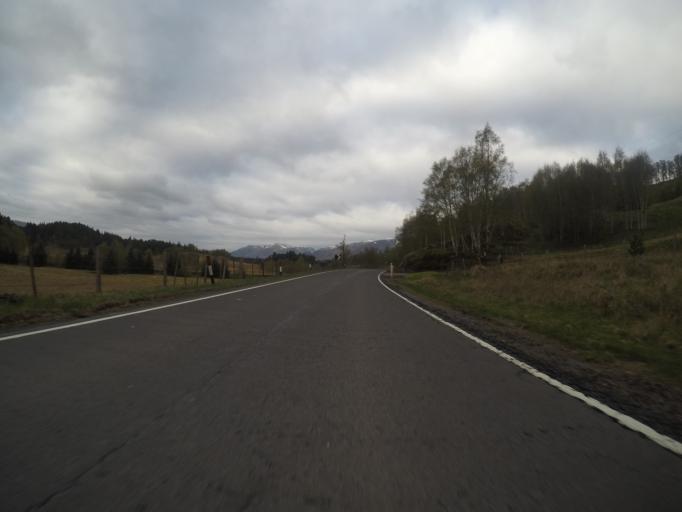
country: GB
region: Scotland
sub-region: Highland
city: Kingussie
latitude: 56.9757
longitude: -4.3908
